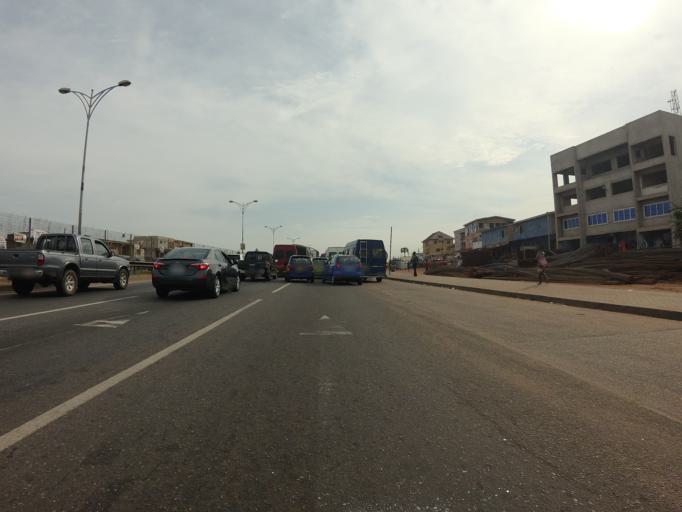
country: GH
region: Greater Accra
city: Dome
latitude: 5.6024
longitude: -0.2588
